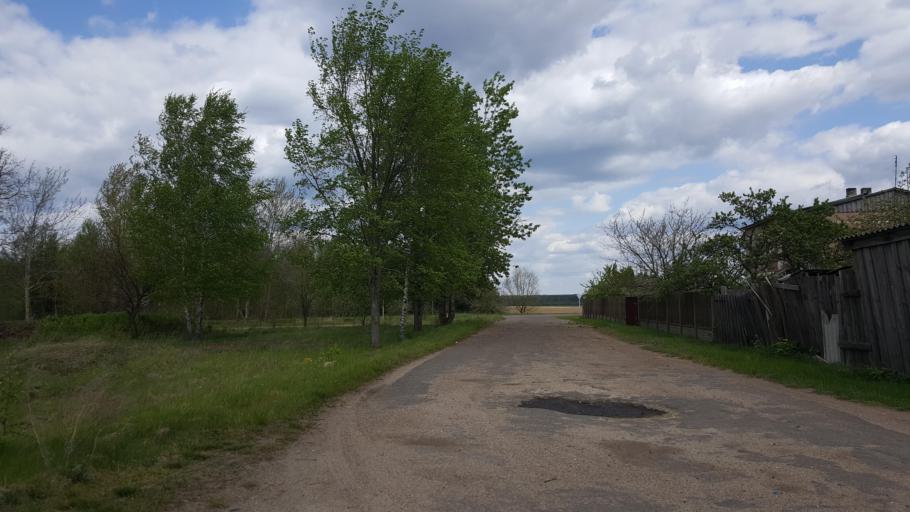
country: BY
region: Brest
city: Kamyanyets
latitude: 52.3932
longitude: 23.9948
